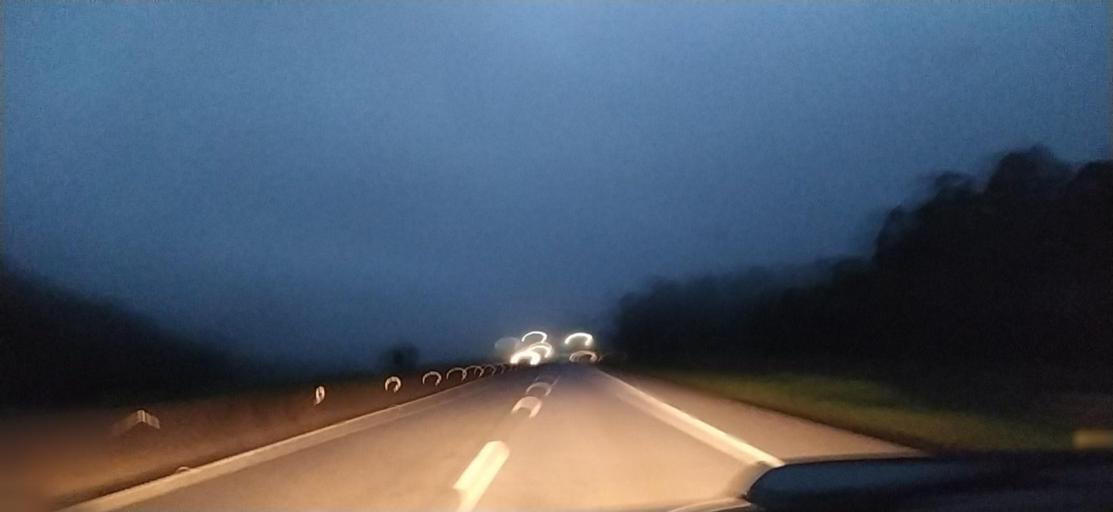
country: BR
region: Minas Gerais
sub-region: Sao Goncalo Do Sapucai
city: Sao Goncalo do Sapucai
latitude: -21.9870
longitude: -45.6575
